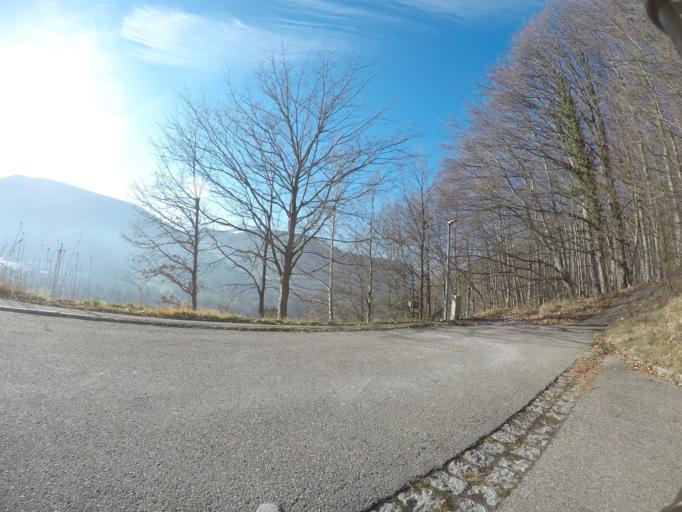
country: DE
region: Baden-Wuerttemberg
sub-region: Tuebingen Region
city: Pfullingen
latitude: 48.4489
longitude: 9.2526
